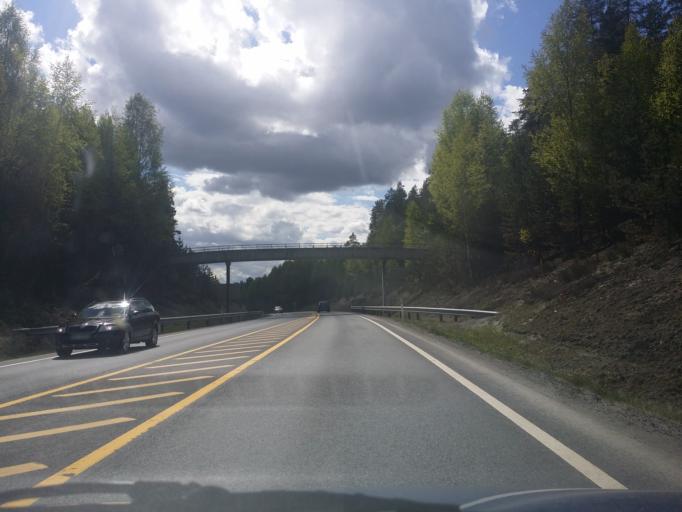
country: NO
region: Buskerud
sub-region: Modum
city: Vikersund
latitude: 59.9402
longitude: 9.9634
